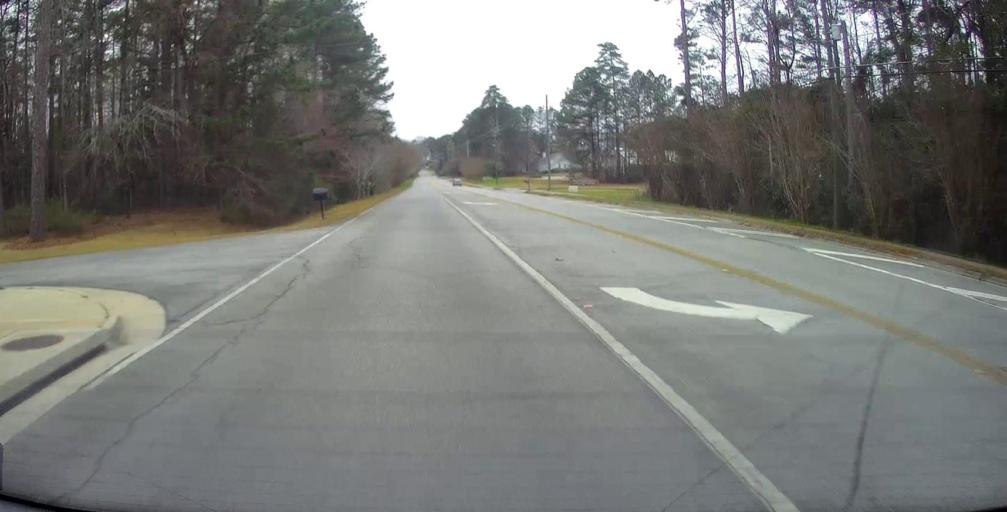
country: US
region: Georgia
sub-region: Bibb County
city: Macon
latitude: 32.9038
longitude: -83.7215
